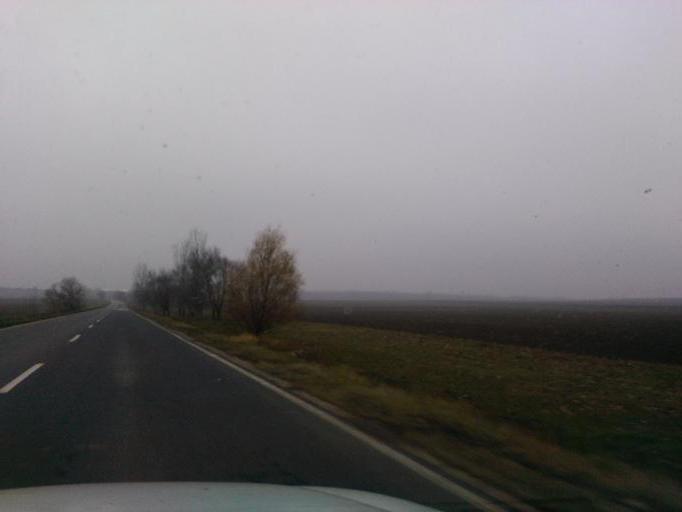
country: HU
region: Pest
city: Tarnok
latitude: 47.3813
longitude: 18.8271
